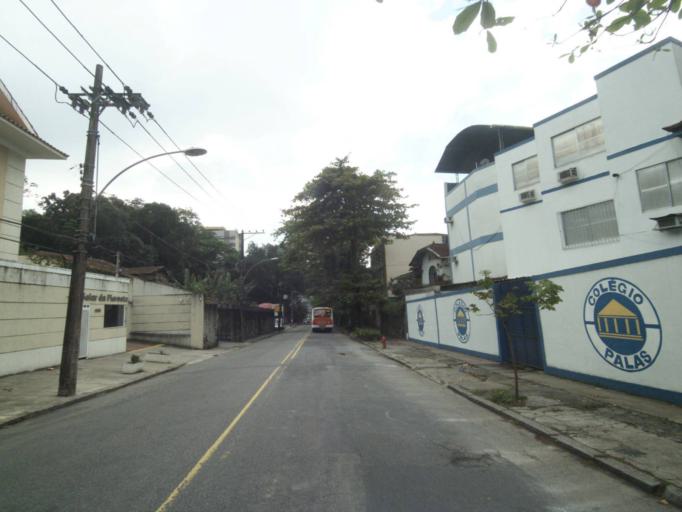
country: BR
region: Rio de Janeiro
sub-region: Rio De Janeiro
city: Rio de Janeiro
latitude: -22.9446
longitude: -43.2558
